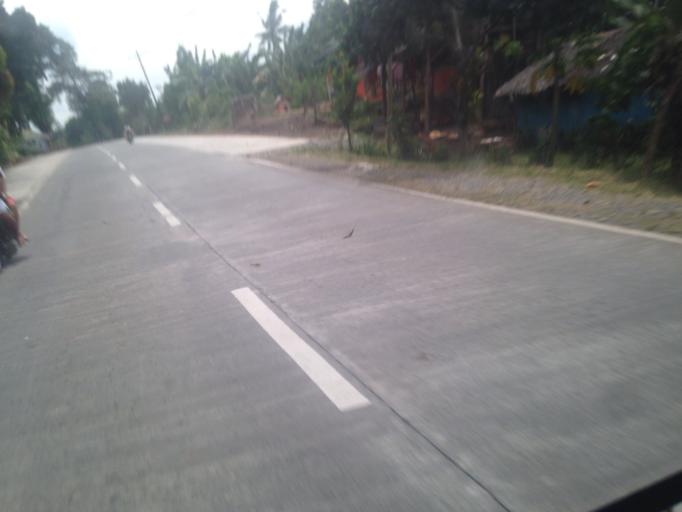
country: PH
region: Mimaropa
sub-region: Province of Mindoro Oriental
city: Saaban
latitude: 13.1106
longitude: 121.3150
